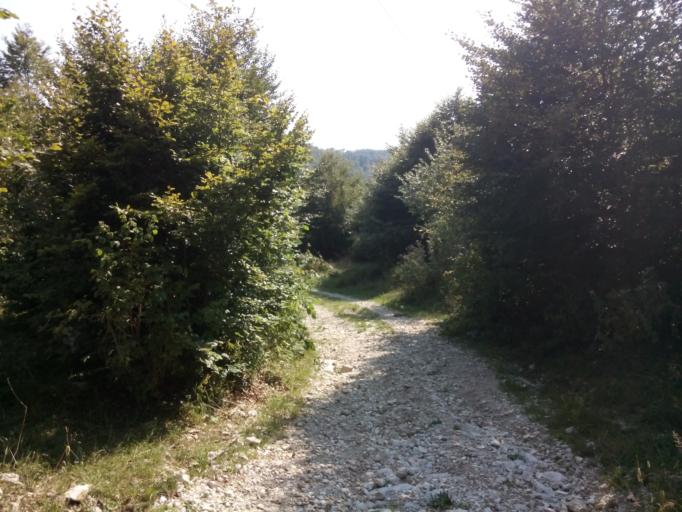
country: IT
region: Veneto
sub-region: Provincia di Vicenza
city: Conco
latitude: 45.8249
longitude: 11.6190
